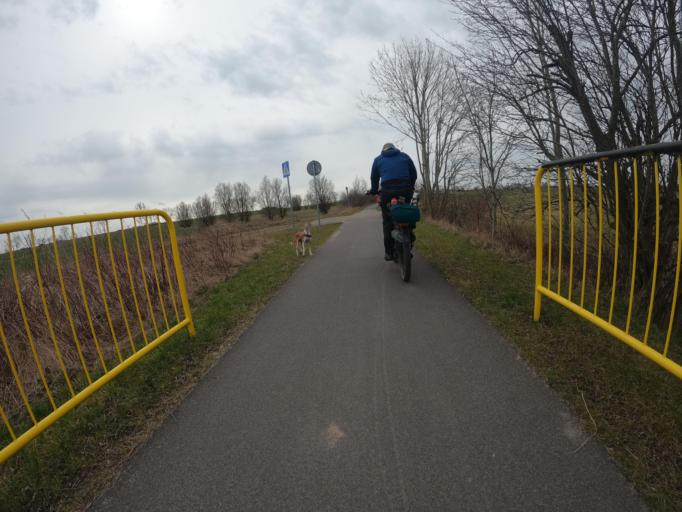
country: PL
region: West Pomeranian Voivodeship
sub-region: Powiat gryficki
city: Trzebiatow
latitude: 54.0953
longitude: 15.2771
